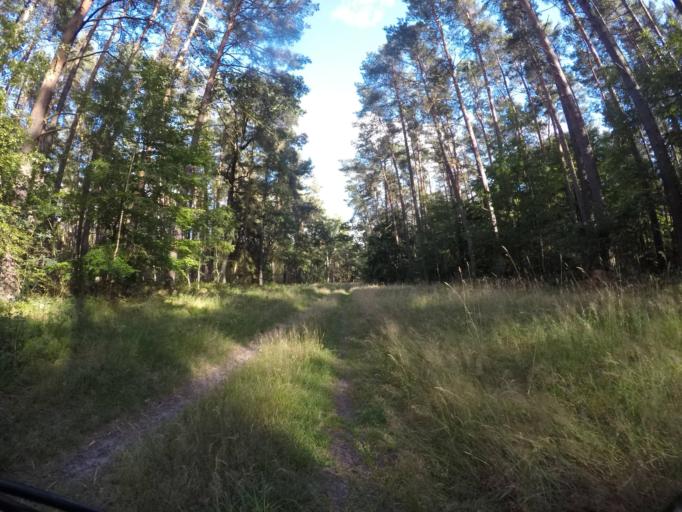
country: DE
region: Mecklenburg-Vorpommern
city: Lubtheen
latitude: 53.2411
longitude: 11.0210
